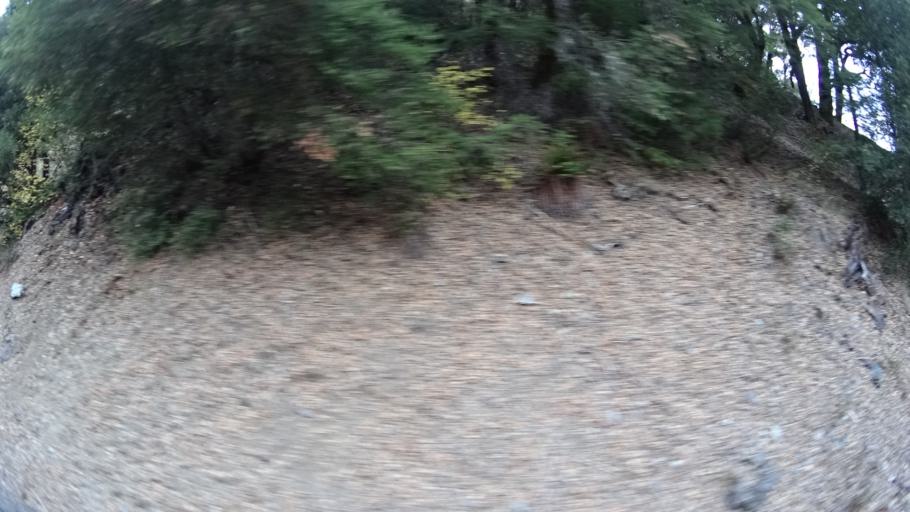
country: US
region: California
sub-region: Siskiyou County
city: Happy Camp
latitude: 41.8884
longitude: -123.4331
